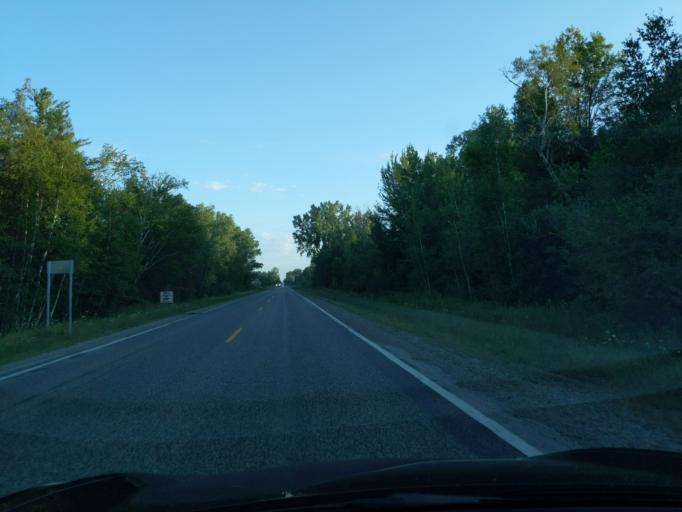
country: US
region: Michigan
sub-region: Gratiot County
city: Breckenridge
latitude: 43.4469
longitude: -84.3700
